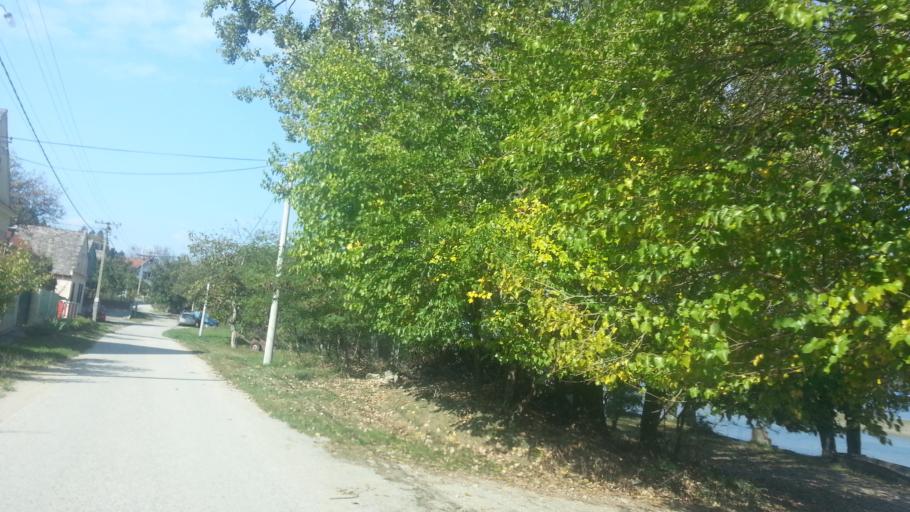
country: RS
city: Novi Slankamen
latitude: 45.1503
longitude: 20.2479
